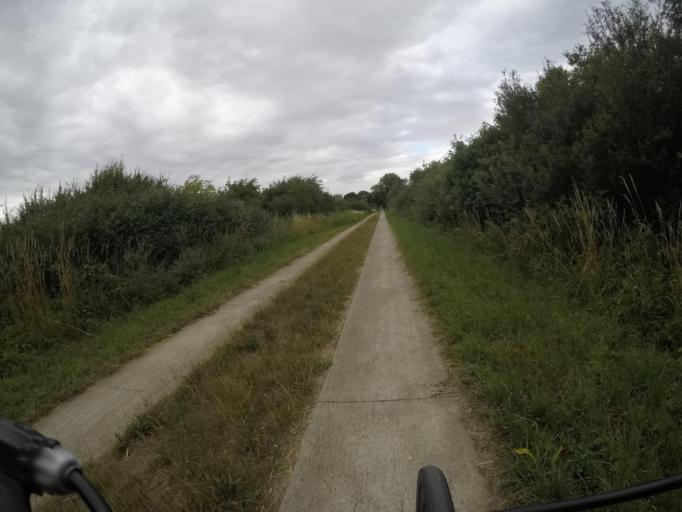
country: DE
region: Lower Saxony
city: Neu Darchau
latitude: 53.2538
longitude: 10.9167
